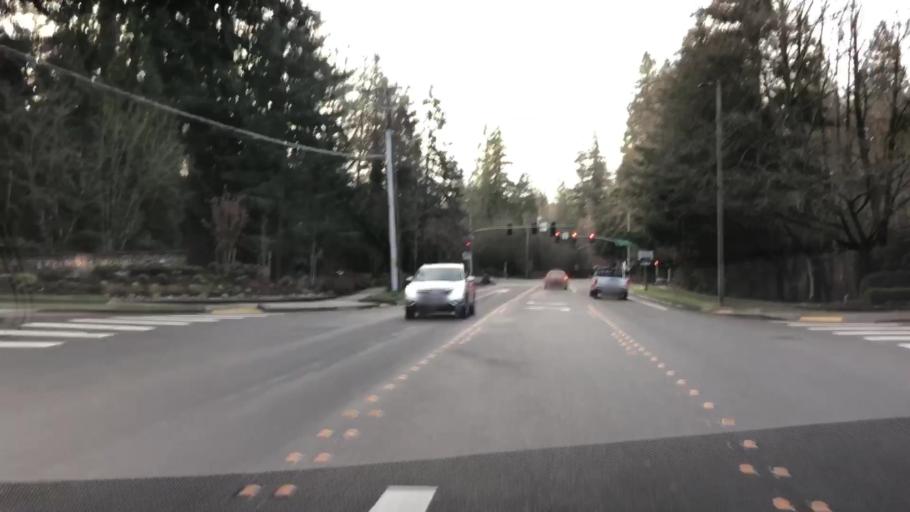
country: US
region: Washington
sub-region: King County
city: Newcastle
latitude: 47.5475
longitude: -122.1293
